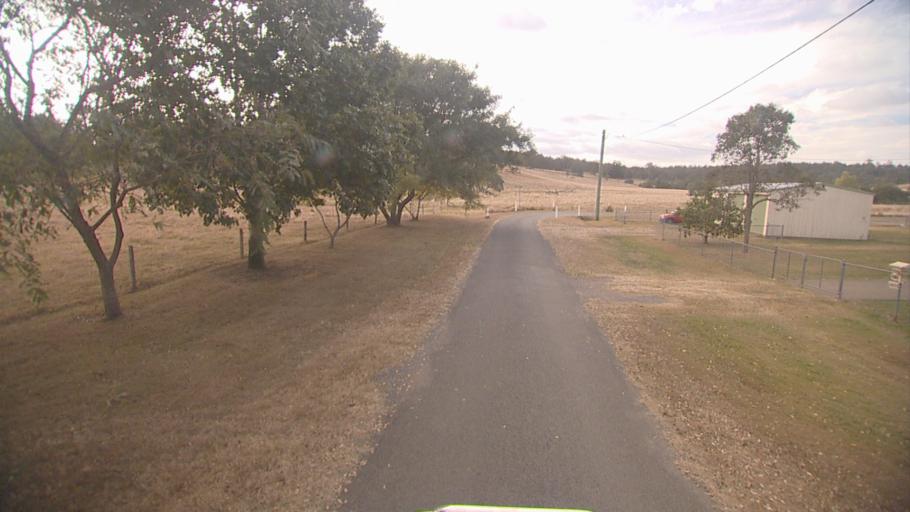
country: AU
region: Queensland
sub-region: Logan
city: Cedar Vale
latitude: -27.9119
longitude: 152.9868
